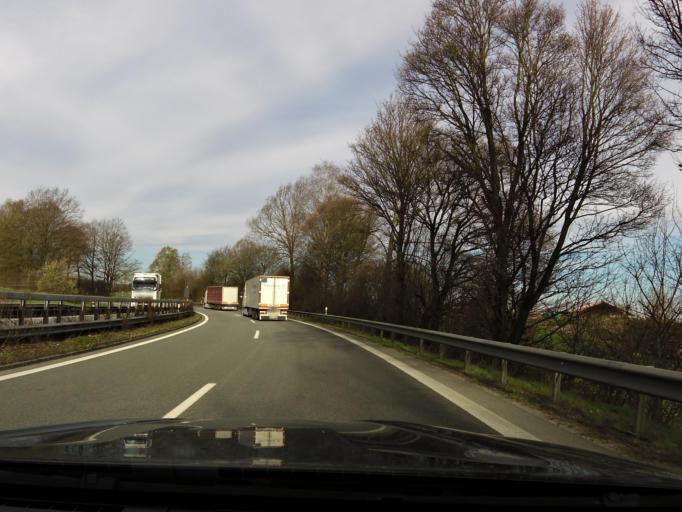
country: DE
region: Bavaria
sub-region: Upper Bavaria
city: Raubling
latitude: 47.8115
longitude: 12.0952
